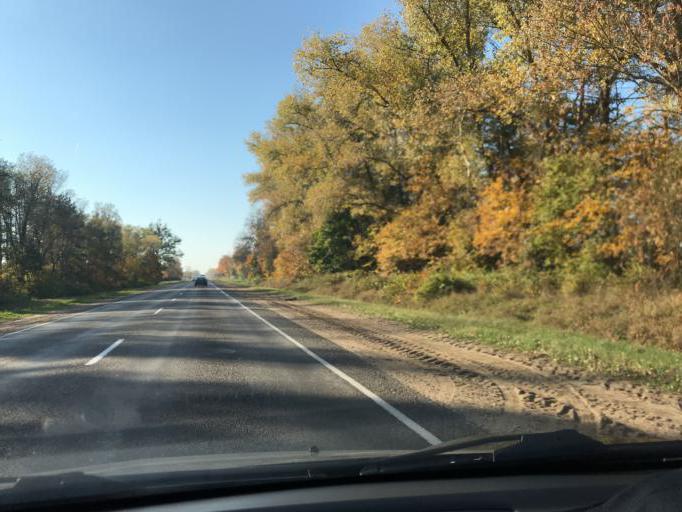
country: BY
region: Mogilev
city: Hlusha
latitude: 53.0935
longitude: 28.9472
